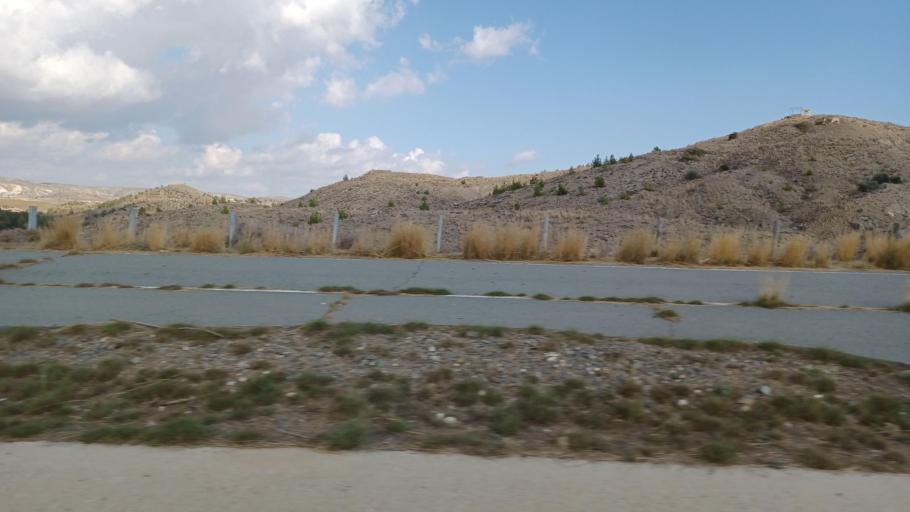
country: CY
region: Larnaka
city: Troulloi
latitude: 35.0094
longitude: 33.6246
